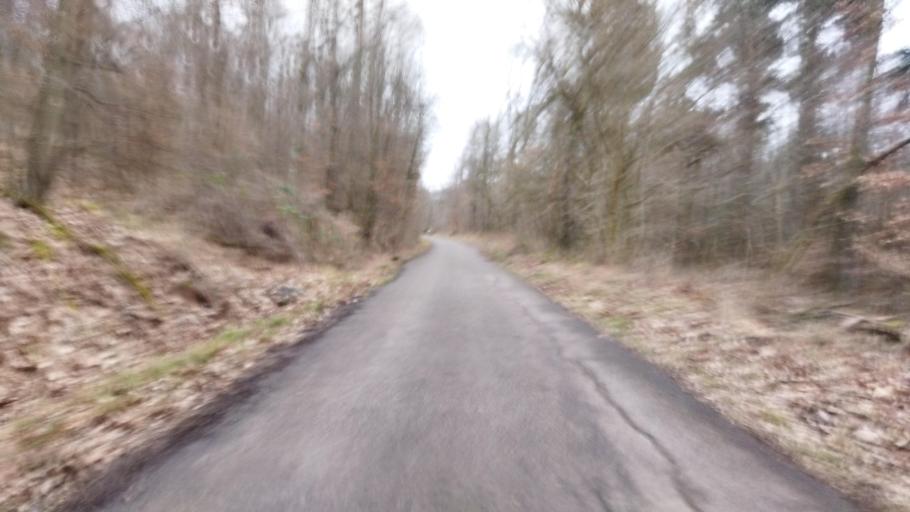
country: DE
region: Baden-Wuerttemberg
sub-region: Regierungsbezirk Stuttgart
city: Untergruppenbach
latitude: 49.1093
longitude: 9.2487
